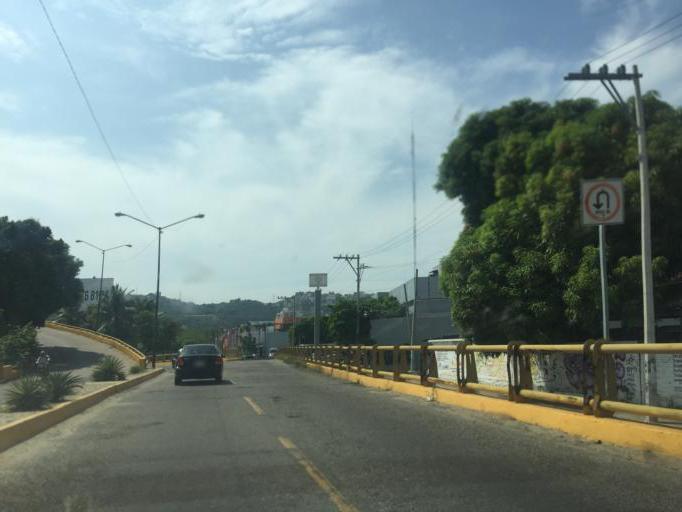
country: MX
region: Guerrero
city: Acapulco de Juarez
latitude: 16.8581
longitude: -99.9061
